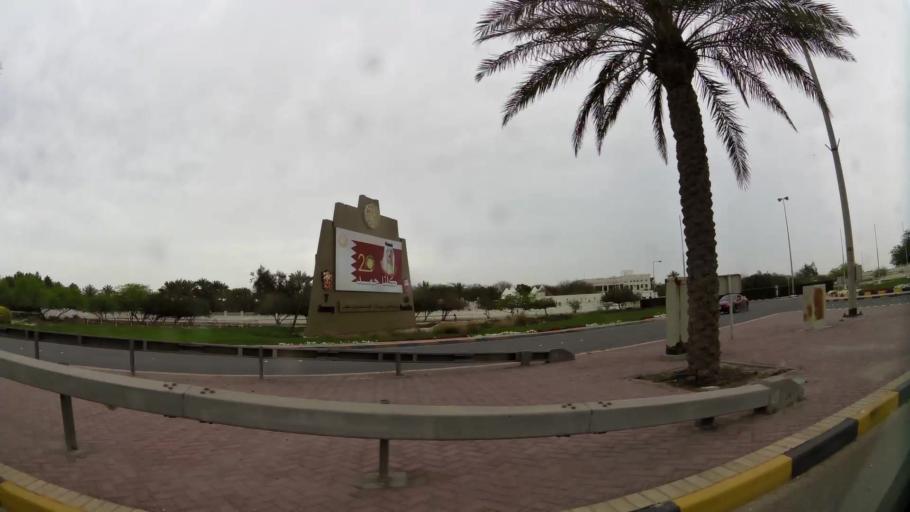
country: BH
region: Northern
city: Ar Rifa'
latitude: 26.1085
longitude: 50.5392
